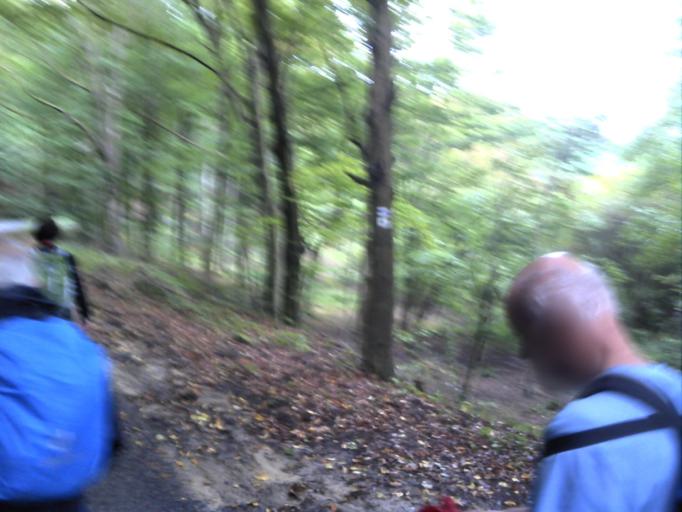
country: HU
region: Borsod-Abauj-Zemplen
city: Satoraljaujhely
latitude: 48.4018
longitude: 21.6045
